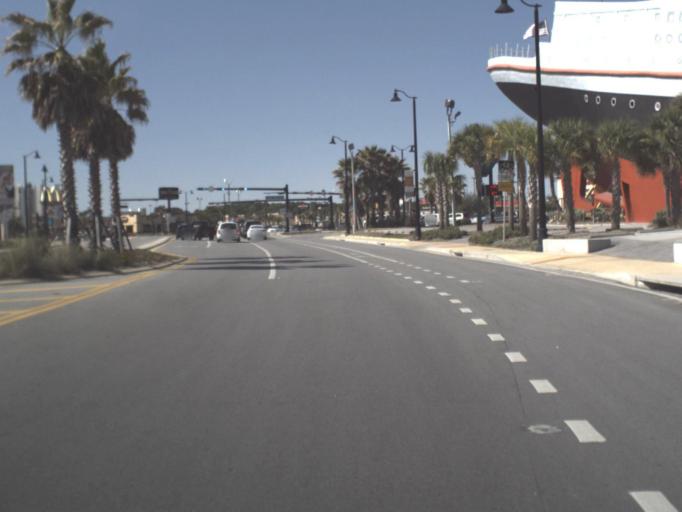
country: US
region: Florida
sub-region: Bay County
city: Panama City Beach
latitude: 30.1778
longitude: -85.7990
